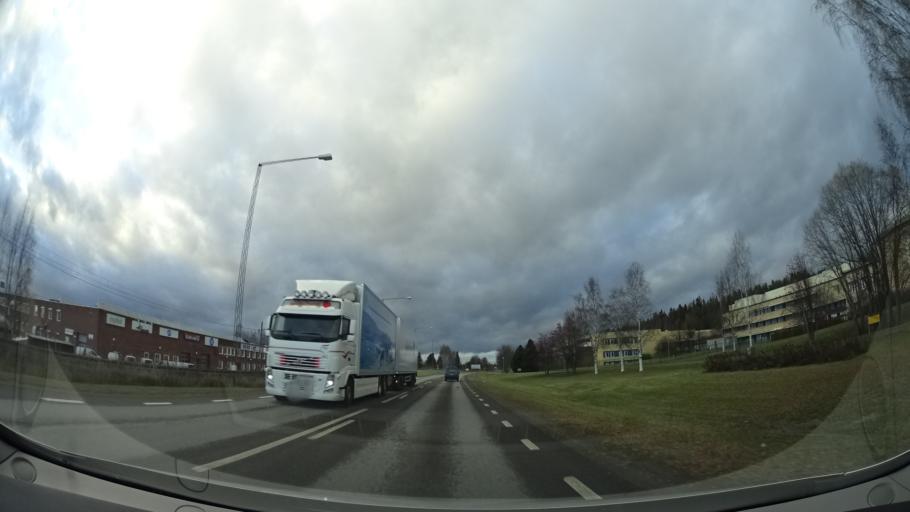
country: SE
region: Vaesterbotten
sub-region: Skelleftea Kommun
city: Skelleftea
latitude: 64.7551
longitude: 20.9423
